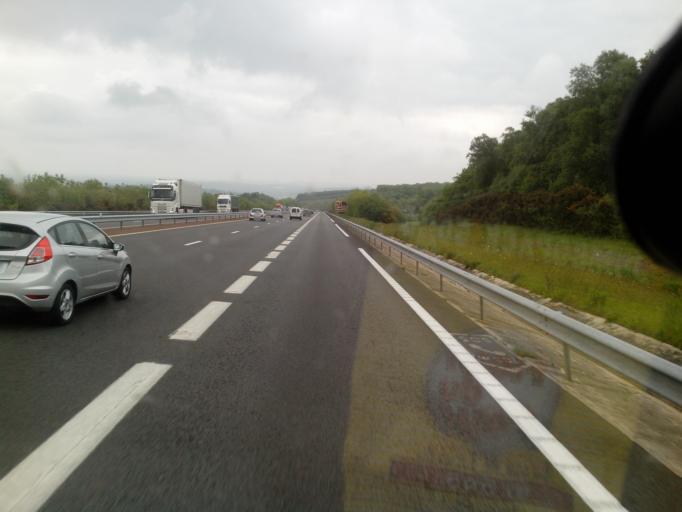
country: FR
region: Lower Normandy
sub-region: Departement de la Manche
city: Tessy-sur-Vire
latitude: 48.9173
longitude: -1.0891
